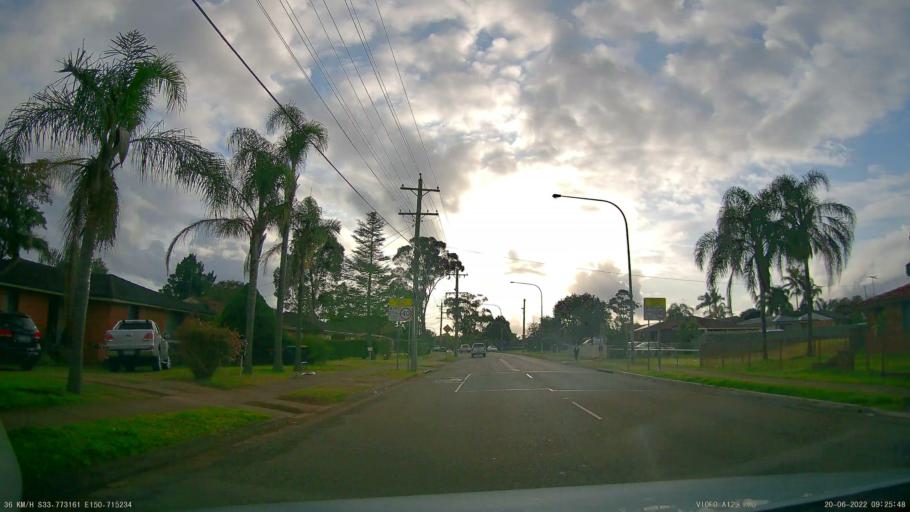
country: AU
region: New South Wales
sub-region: Penrith Municipality
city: Kingswood Park
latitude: -33.7731
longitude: 150.7154
